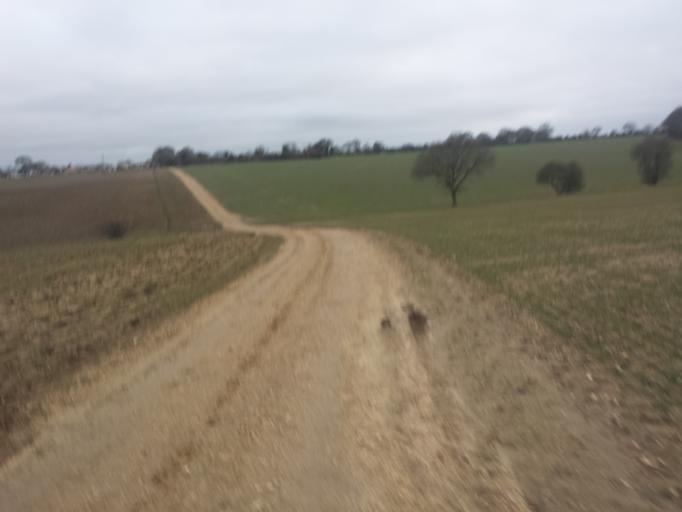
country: GB
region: England
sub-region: Essex
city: Little Clacton
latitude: 51.8464
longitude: 1.1492
